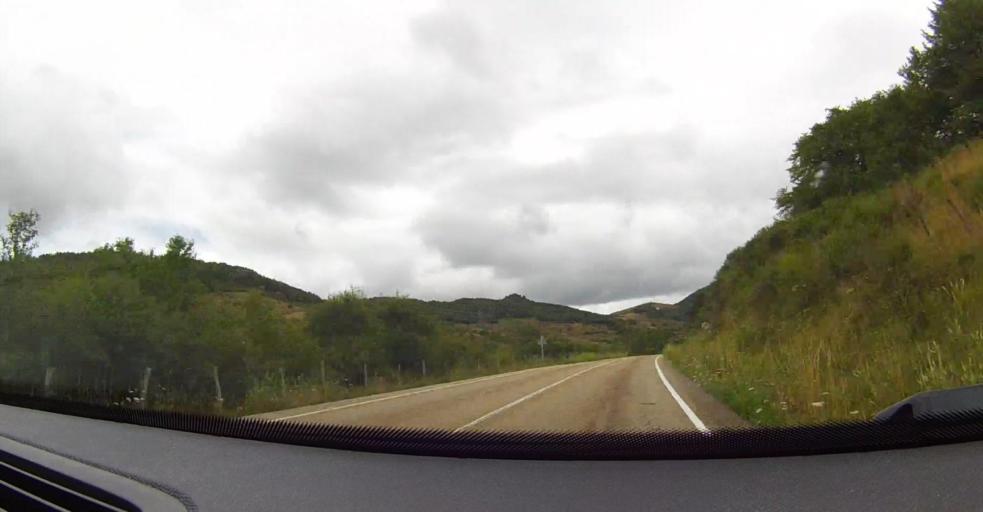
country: ES
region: Castille and Leon
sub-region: Provincia de Leon
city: Reyero
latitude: 42.9441
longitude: -5.2449
